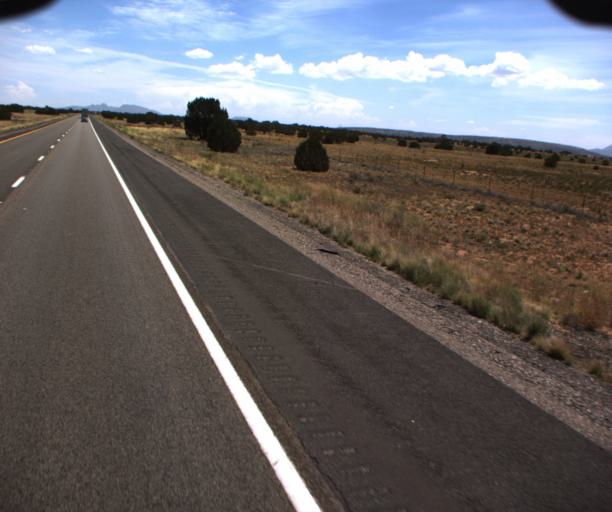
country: US
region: Arizona
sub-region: Mohave County
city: Peach Springs
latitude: 35.3133
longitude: -112.9699
